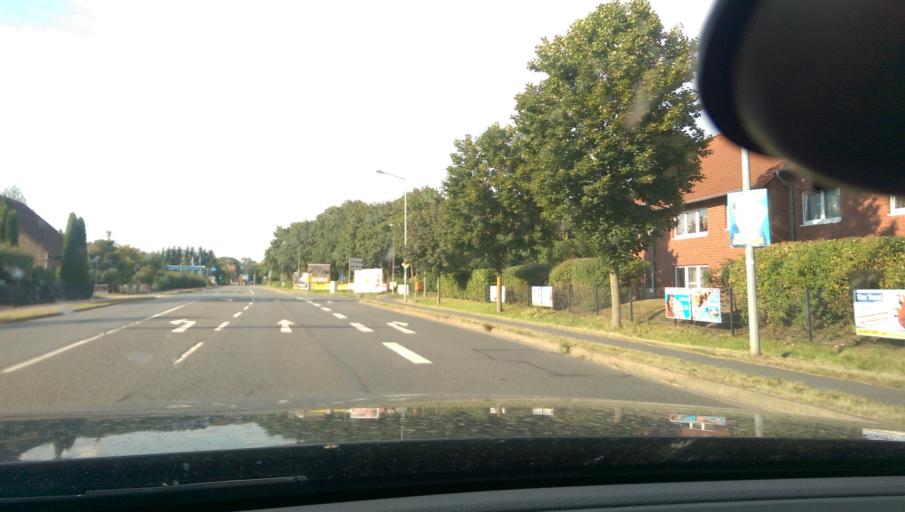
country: DE
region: Lower Saxony
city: Neustadt am Rubenberge
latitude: 52.4935
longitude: 9.4566
